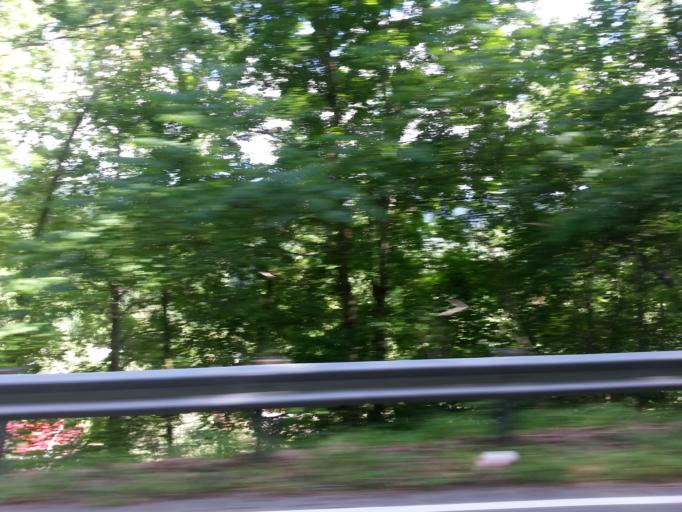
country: US
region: Kentucky
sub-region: Harlan County
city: Harlan
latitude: 36.8918
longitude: -83.2800
